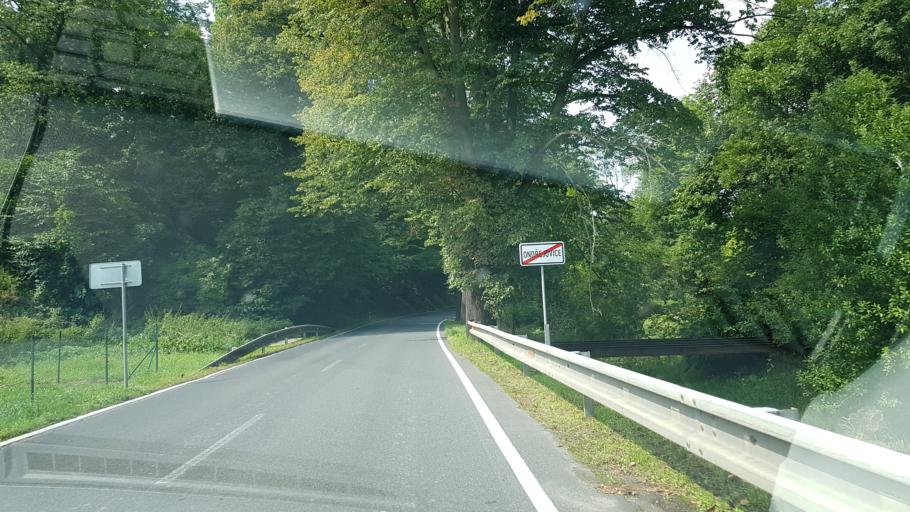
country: CZ
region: Olomoucky
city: Zlate Hory
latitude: 50.2637
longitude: 17.3509
